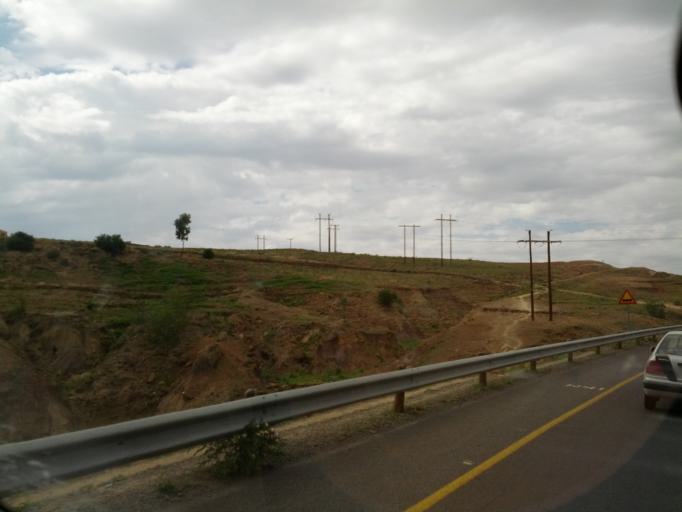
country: LS
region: Maseru
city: Maseru
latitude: -29.3821
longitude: 27.5036
